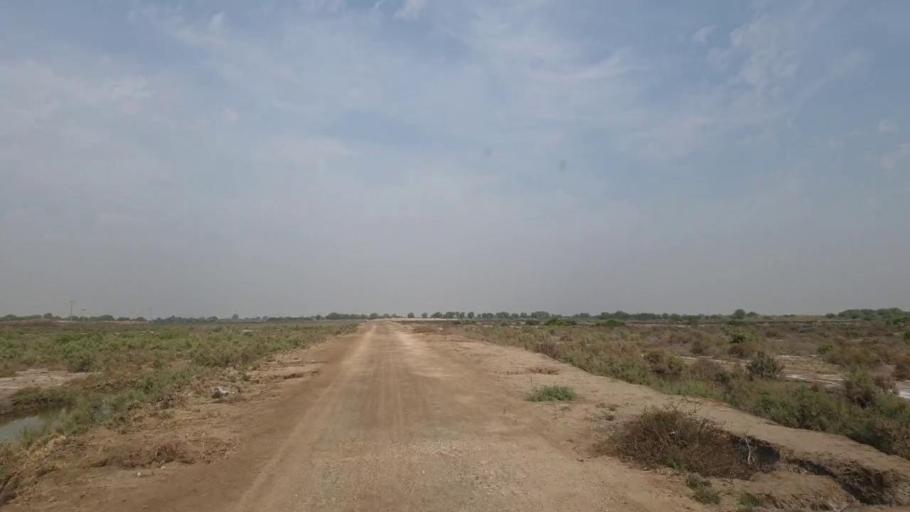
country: PK
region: Sindh
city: Rajo Khanani
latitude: 24.9936
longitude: 68.9951
